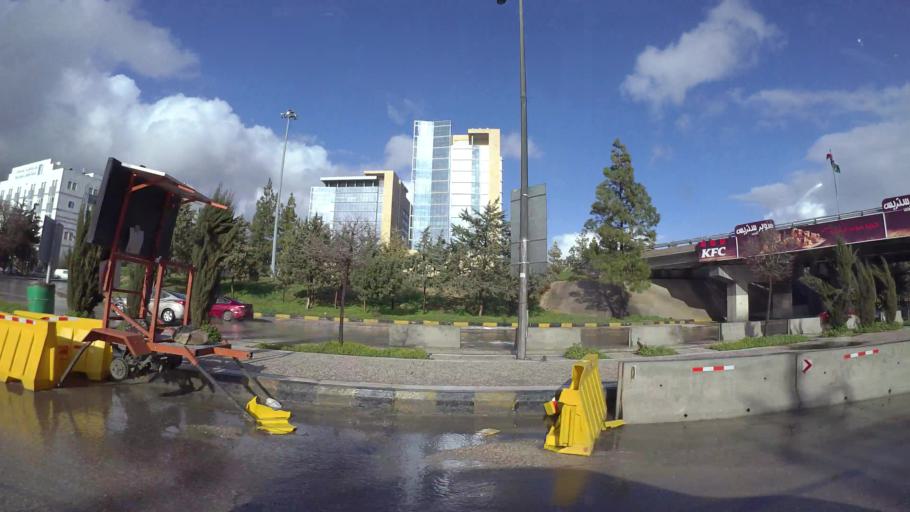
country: JO
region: Amman
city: Al Jubayhah
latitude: 32.0030
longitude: 35.8747
